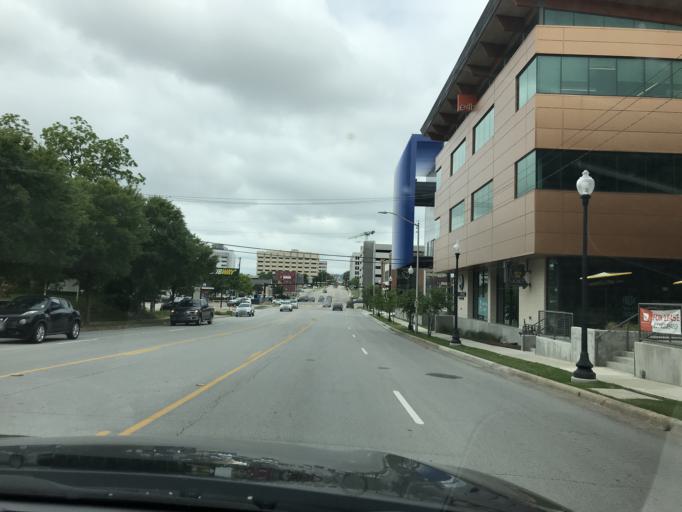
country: US
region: Texas
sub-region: Tarrant County
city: Fort Worth
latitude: 32.7315
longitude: -97.3435
